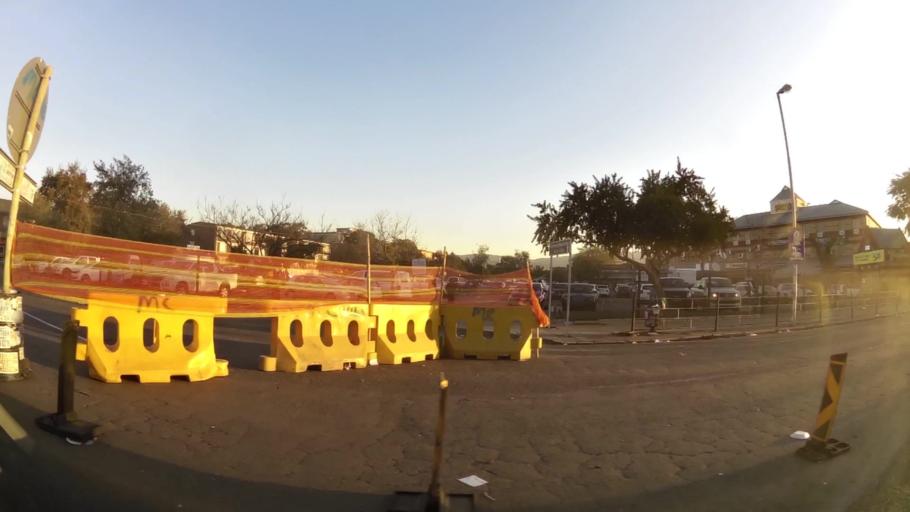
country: ZA
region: North-West
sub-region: Bojanala Platinum District Municipality
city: Rustenburg
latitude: -25.6686
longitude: 27.2392
